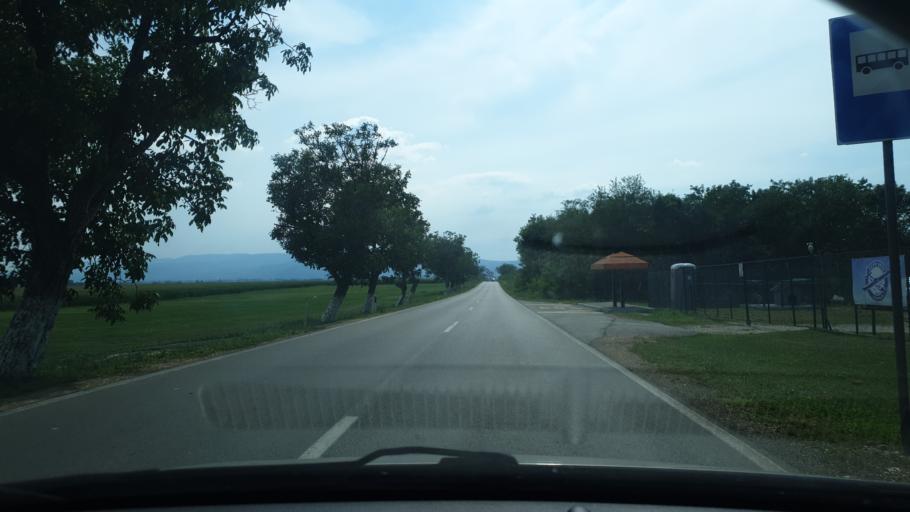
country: RS
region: Central Serbia
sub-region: Pomoravski Okrug
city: Cuprija
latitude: 43.9412
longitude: 21.4092
